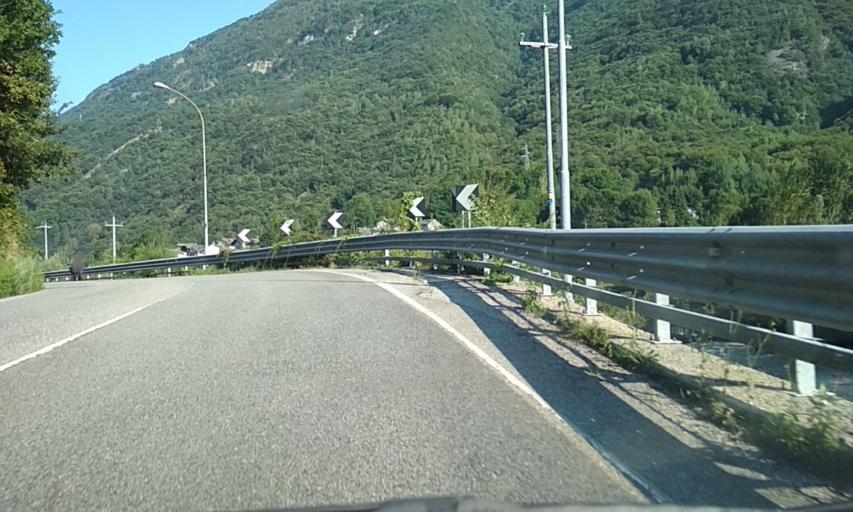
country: IT
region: Piedmont
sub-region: Provincia di Torino
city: Sparone
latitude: 45.4096
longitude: 7.5377
